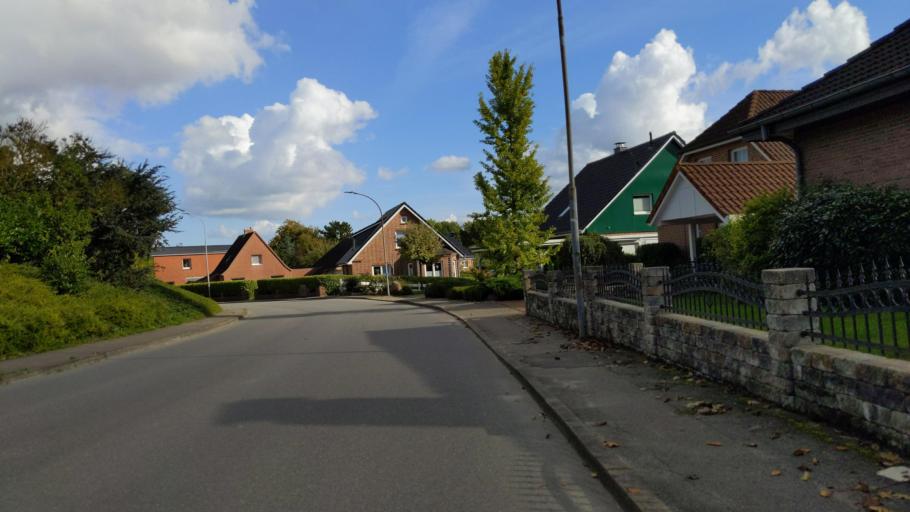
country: DE
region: Schleswig-Holstein
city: Ahrensbok
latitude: 54.0121
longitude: 10.5759
